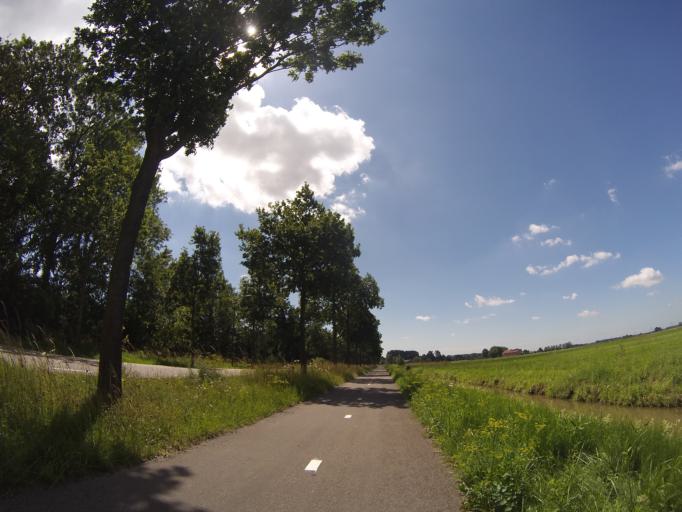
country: NL
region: Utrecht
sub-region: Stichtse Vecht
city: Spechtenkamp
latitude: 52.1283
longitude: 4.9843
